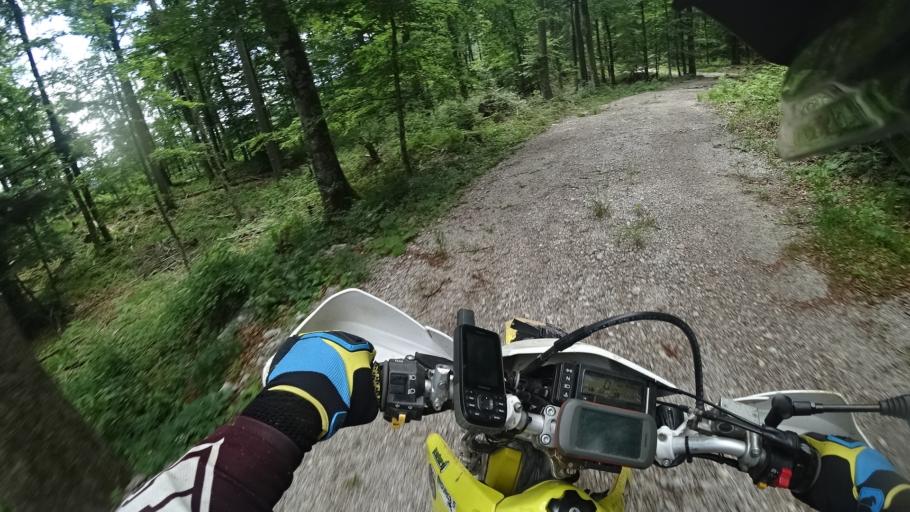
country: SI
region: Osilnica
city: Osilnica
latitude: 45.5056
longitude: 14.6245
